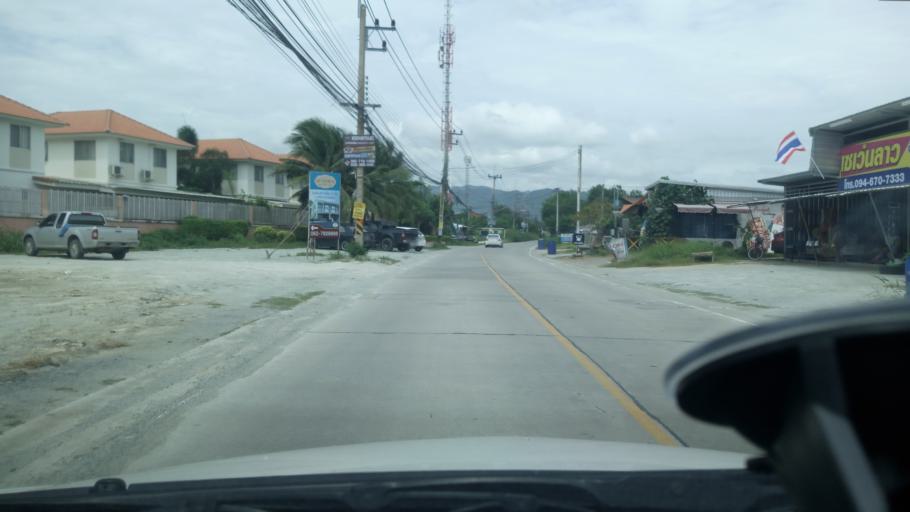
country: TH
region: Chon Buri
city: Chon Buri
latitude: 13.2961
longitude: 100.9592
